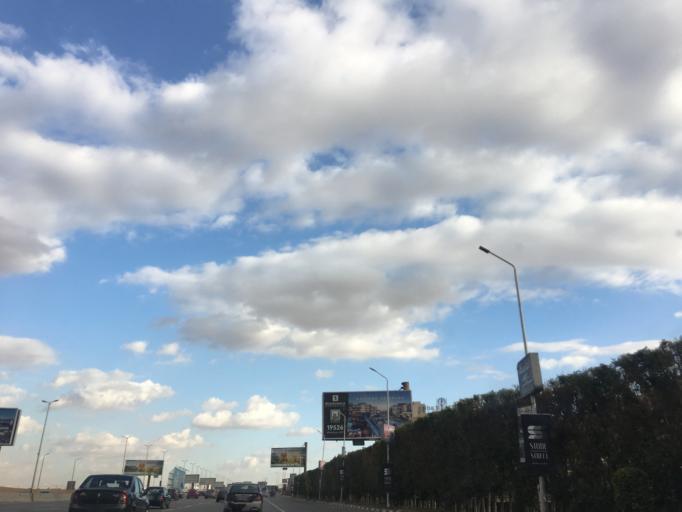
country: EG
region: Muhafazat al Qahirah
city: Cairo
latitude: 30.0213
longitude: 31.3744
